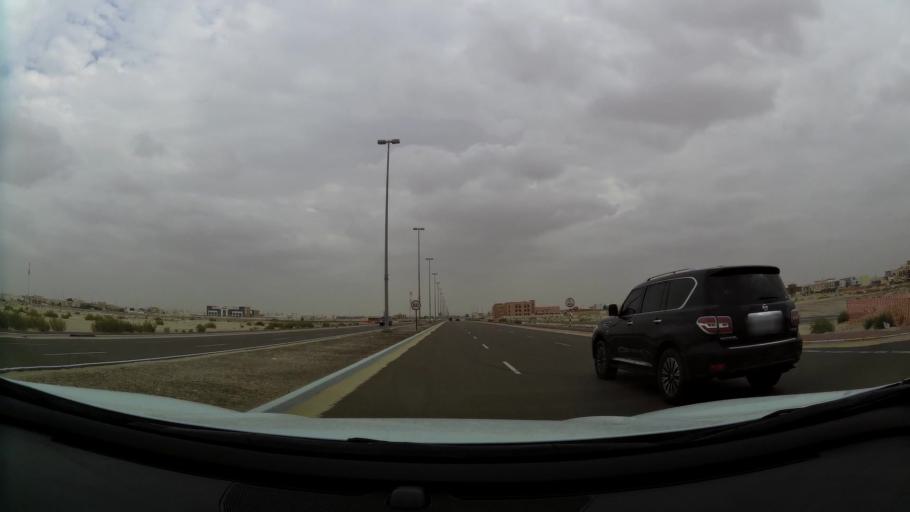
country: AE
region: Abu Dhabi
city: Abu Dhabi
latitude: 24.3647
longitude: 54.6297
